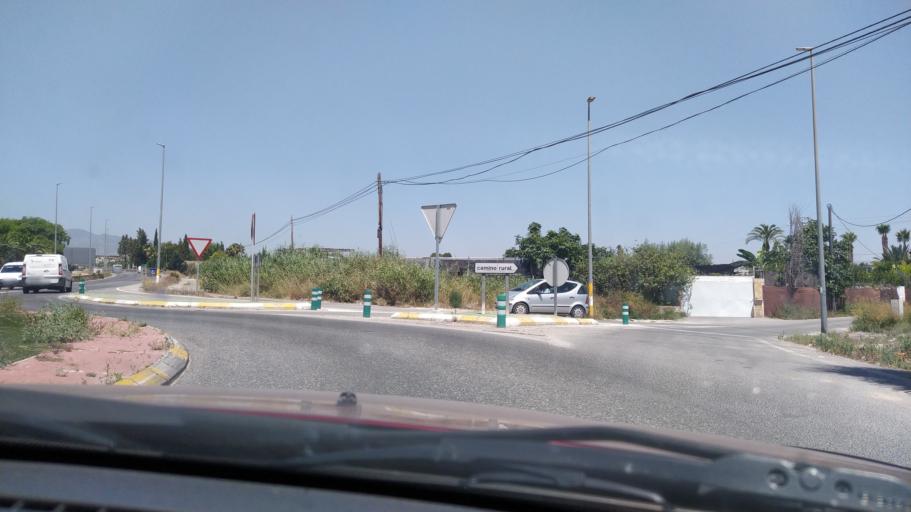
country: ES
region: Murcia
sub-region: Murcia
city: Ceuti
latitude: 38.0865
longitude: -1.2689
